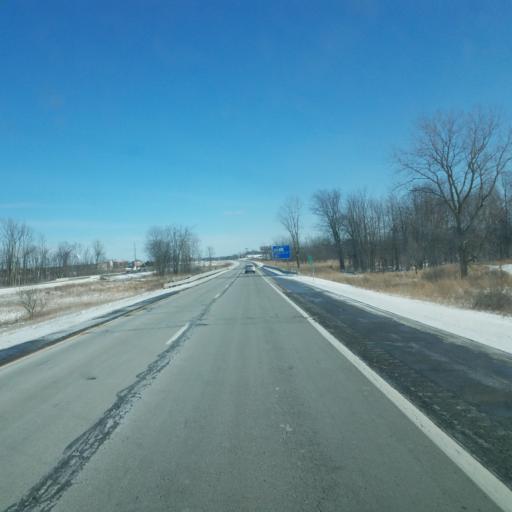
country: US
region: Michigan
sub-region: Livingston County
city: Fowlerville
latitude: 42.6460
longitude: -84.0844
